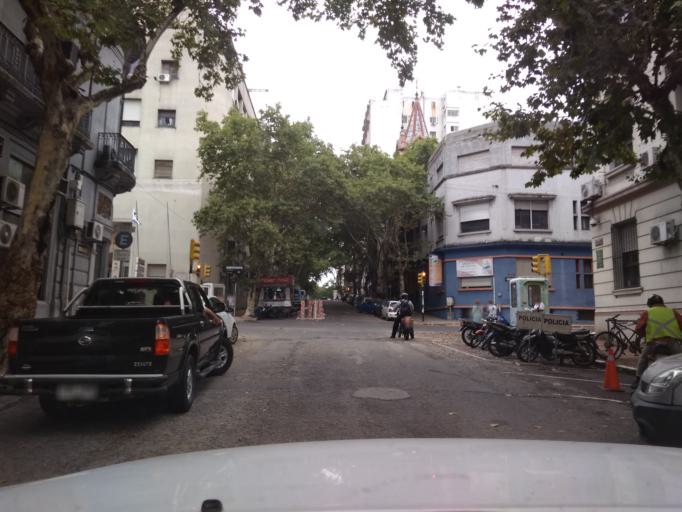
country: UY
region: Montevideo
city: Montevideo
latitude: -34.9040
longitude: -56.1949
